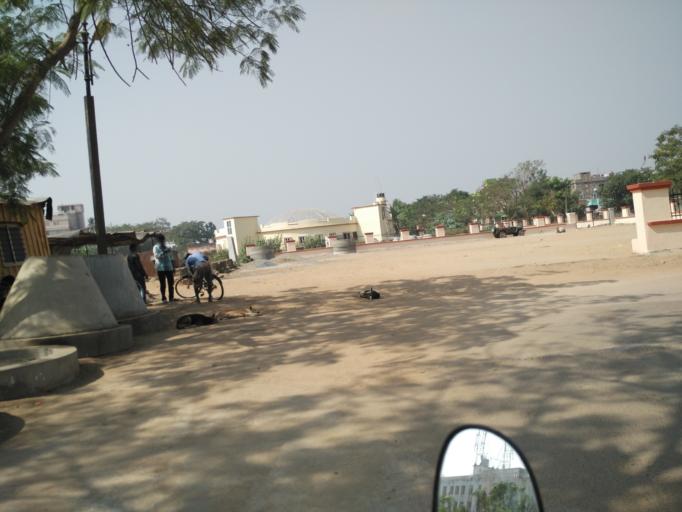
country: IN
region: Odisha
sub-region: Cuttack
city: Cuttack
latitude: 20.4692
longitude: 85.8688
